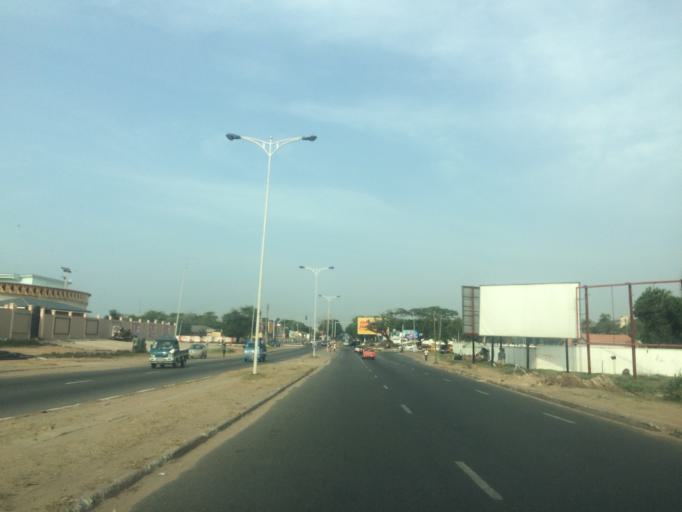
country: GH
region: Greater Accra
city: Accra
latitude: 5.5376
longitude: -0.2200
